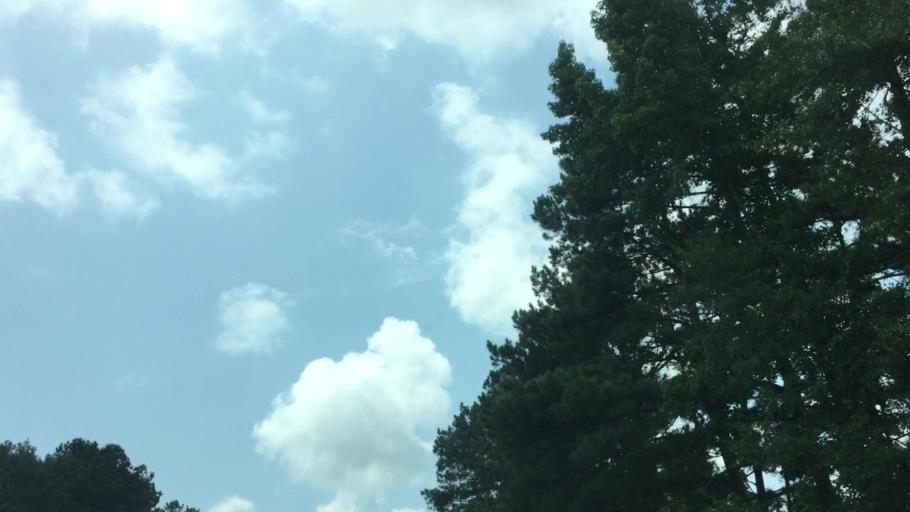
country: US
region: Georgia
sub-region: Fulton County
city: Chattahoochee Hills
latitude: 33.5792
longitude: -84.8131
